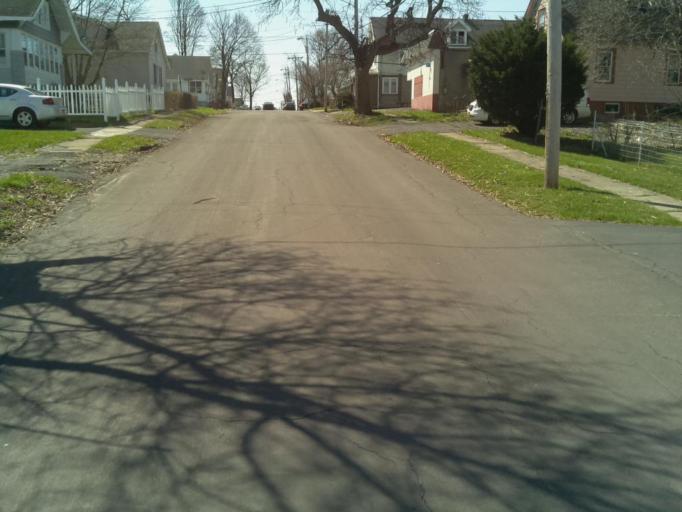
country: US
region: New York
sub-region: Onondaga County
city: Lyncourt
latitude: 43.0732
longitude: -76.1136
